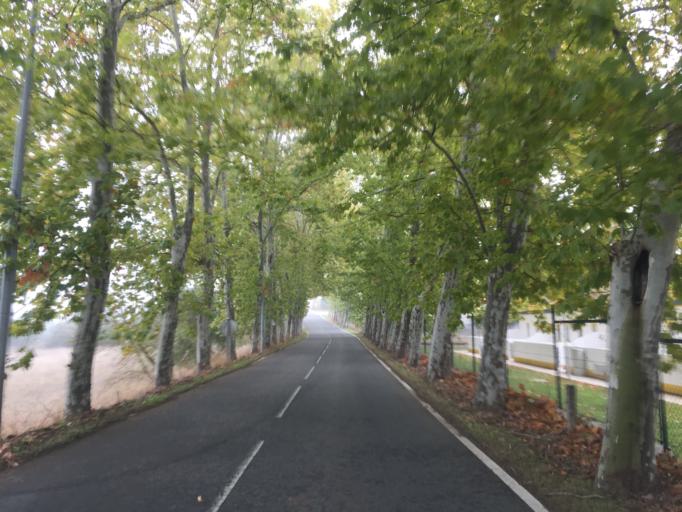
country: PT
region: Portalegre
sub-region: Alter do Chao
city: Alter do Chao
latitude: 39.1368
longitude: -7.5761
